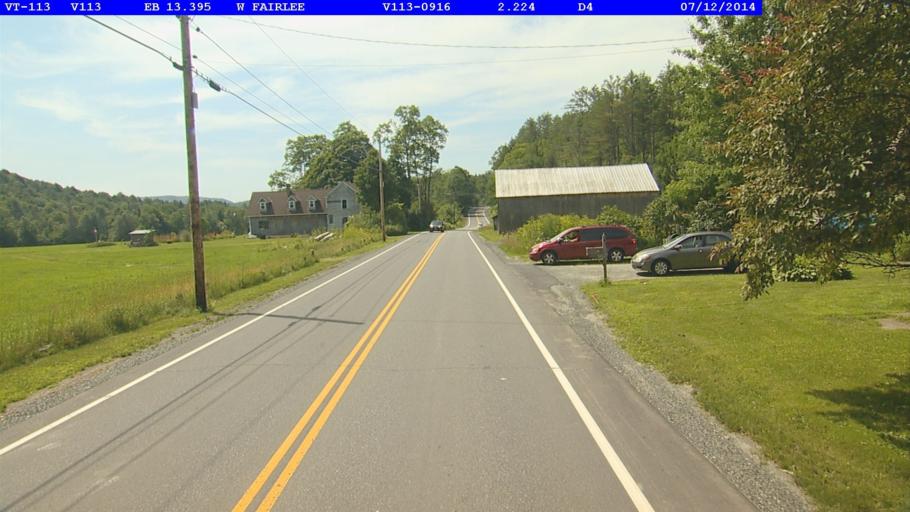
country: US
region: New Hampshire
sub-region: Grafton County
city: Orford
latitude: 43.9056
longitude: -72.2629
